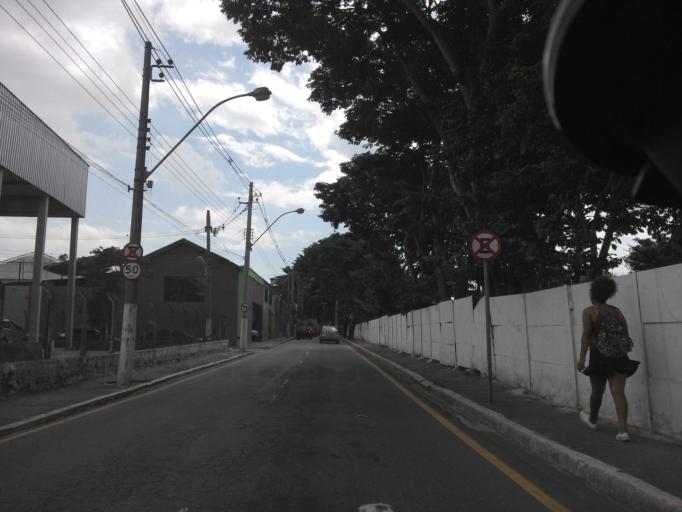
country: BR
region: Sao Paulo
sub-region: Taubate
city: Taubate
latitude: -23.0214
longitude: -45.5583
